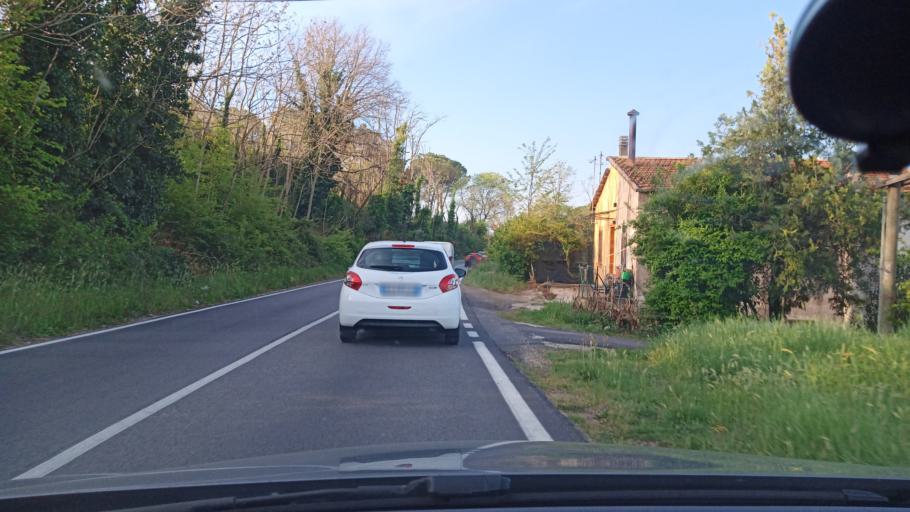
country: IT
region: Latium
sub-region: Citta metropolitana di Roma Capitale
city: Fiano Romano
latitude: 42.1729
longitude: 12.6358
